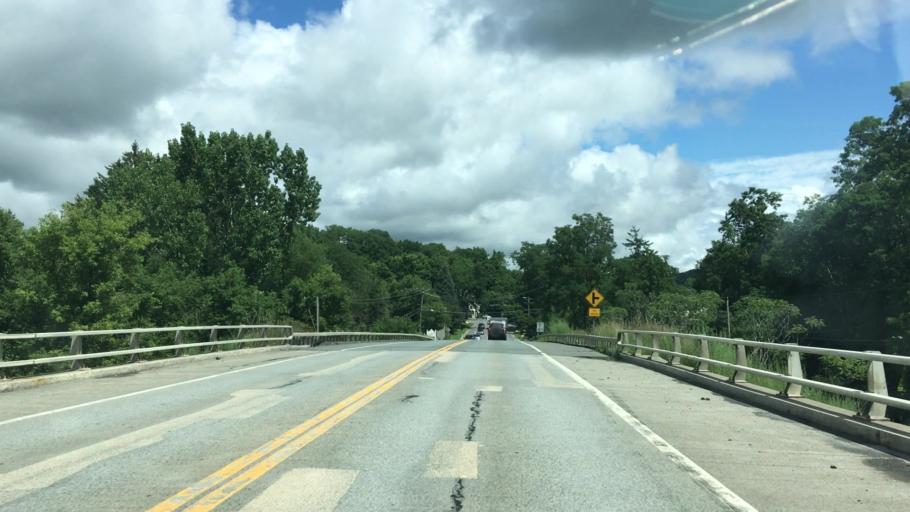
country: US
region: New York
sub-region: Rensselaer County
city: Hoosick Falls
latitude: 42.8613
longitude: -73.3313
